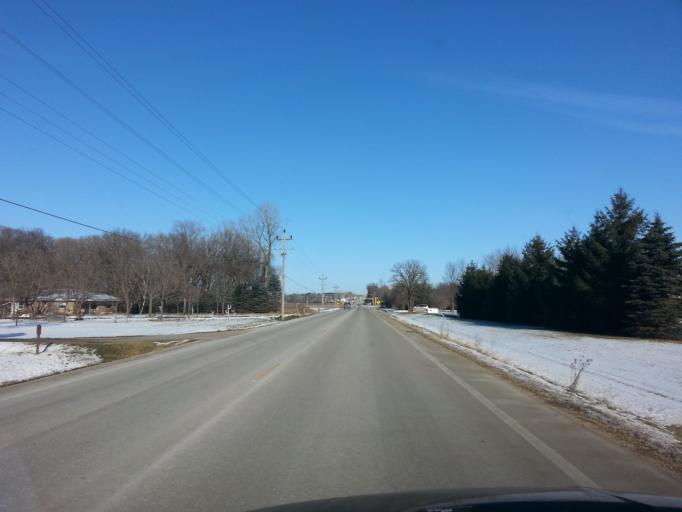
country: US
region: Minnesota
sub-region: Olmsted County
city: Rochester
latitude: 44.0057
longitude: -92.3789
